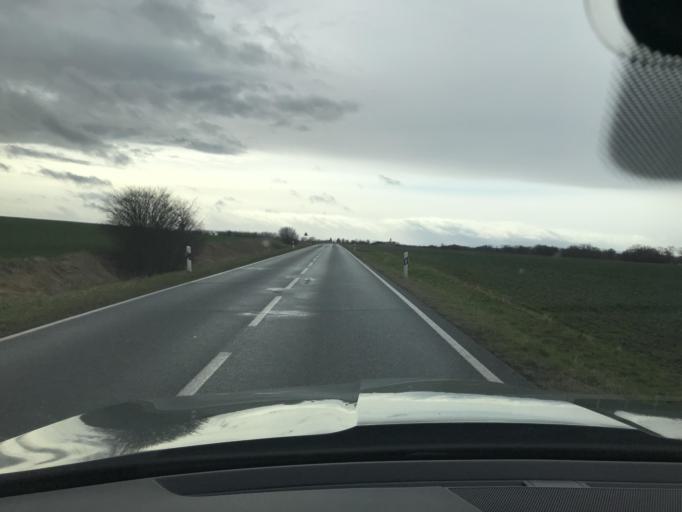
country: DE
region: Saxony-Anhalt
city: Groeningen
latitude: 51.9290
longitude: 11.2051
